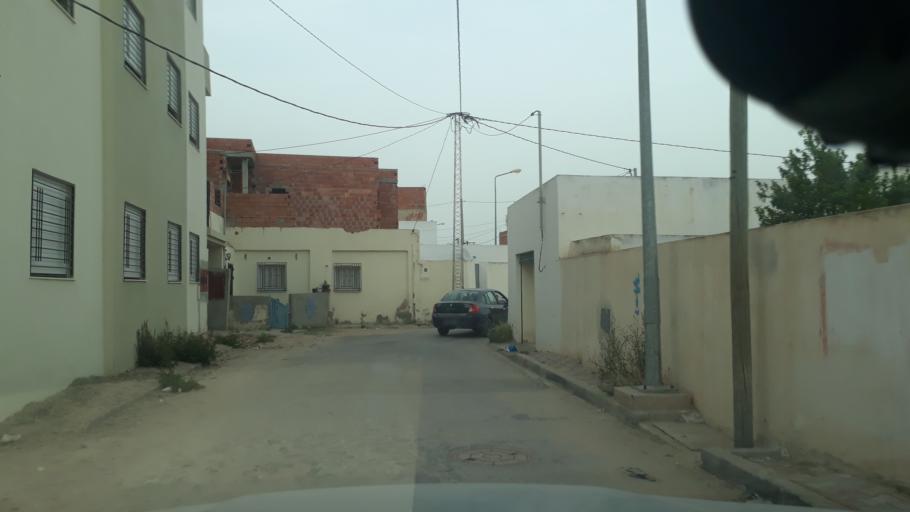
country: TN
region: Safaqis
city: Al Qarmadah
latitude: 34.7773
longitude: 10.7617
